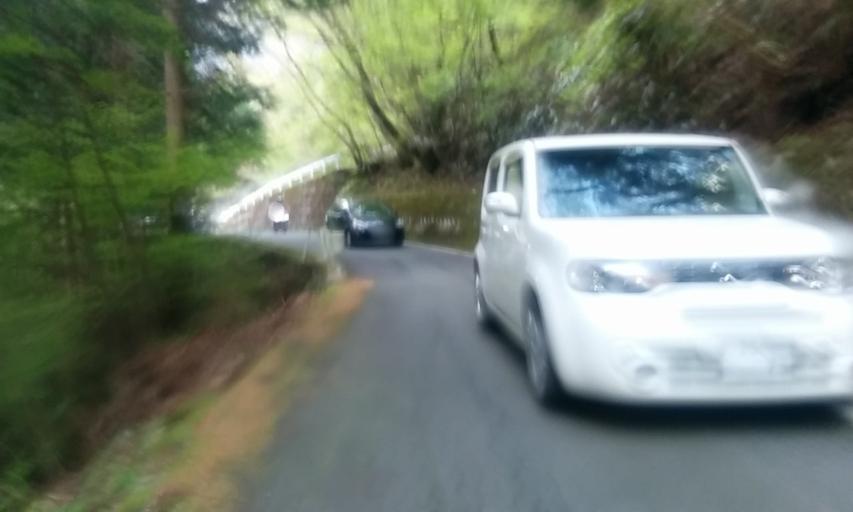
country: JP
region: Ehime
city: Saijo
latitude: 33.8025
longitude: 133.2783
